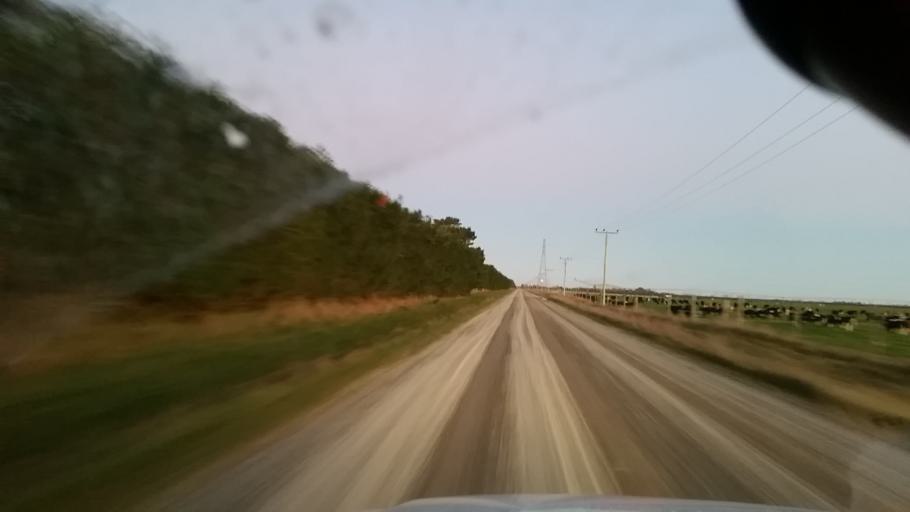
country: NZ
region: Canterbury
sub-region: Ashburton District
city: Tinwald
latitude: -43.9794
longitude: 171.6459
